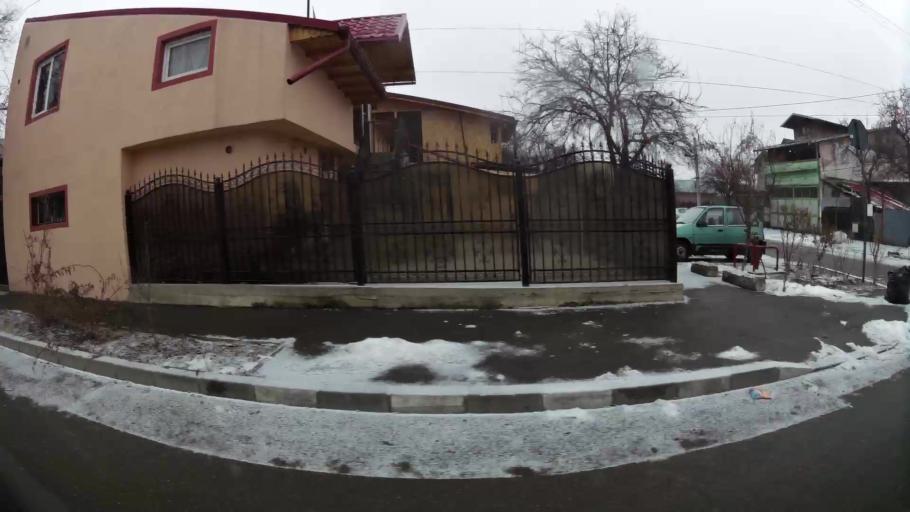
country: RO
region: Prahova
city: Ploiesti
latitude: 44.9545
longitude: 26.0373
